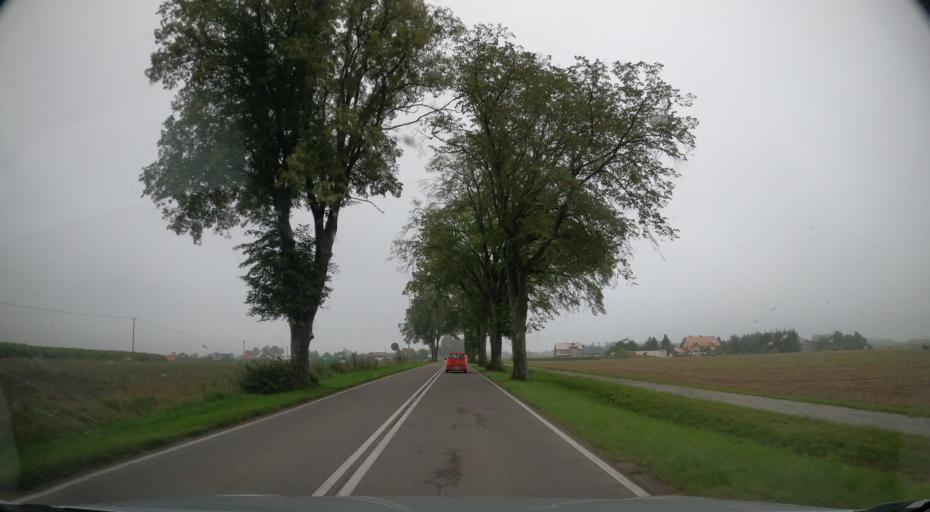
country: PL
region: Pomeranian Voivodeship
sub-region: Powiat wejherowski
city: Bojano
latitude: 54.4529
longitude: 18.3693
